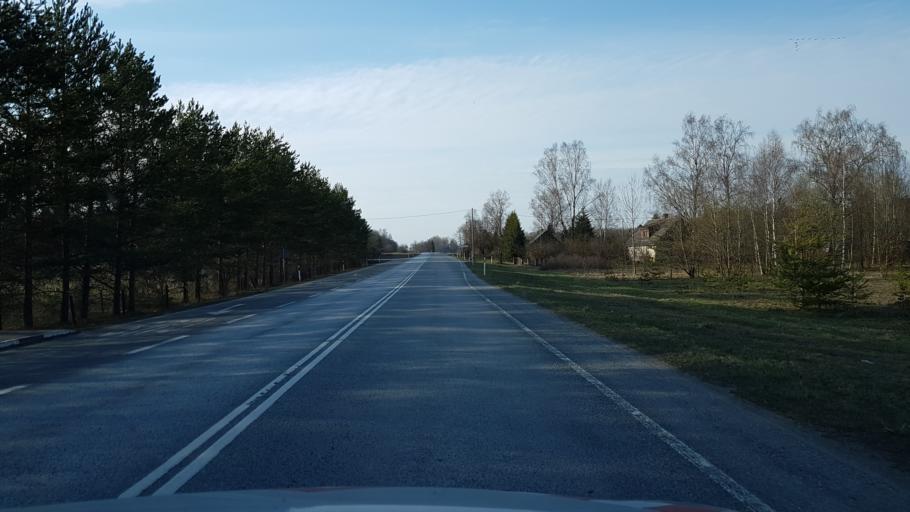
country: EE
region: Laeaene-Virumaa
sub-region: Haljala vald
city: Haljala
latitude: 59.3936
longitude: 26.3105
